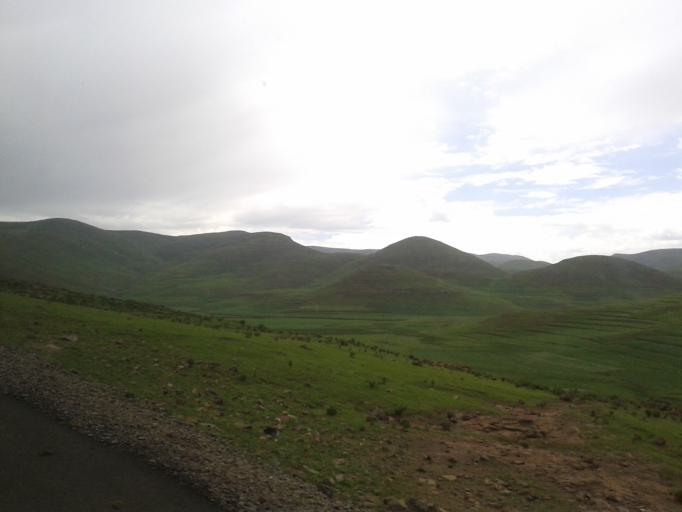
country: LS
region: Maseru
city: Nako
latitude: -29.7775
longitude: 28.0231
